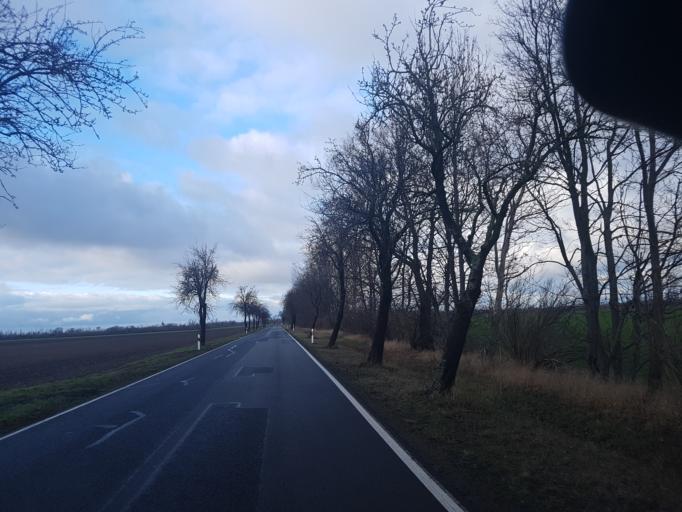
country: DE
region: Brandenburg
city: Muhlberg
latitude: 51.4167
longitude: 13.2343
